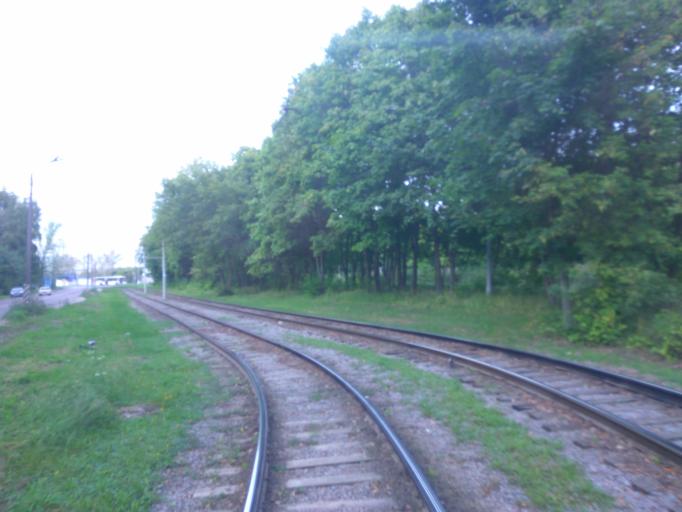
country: RU
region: Moskovskaya
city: Kolomna
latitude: 55.0782
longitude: 38.8167
